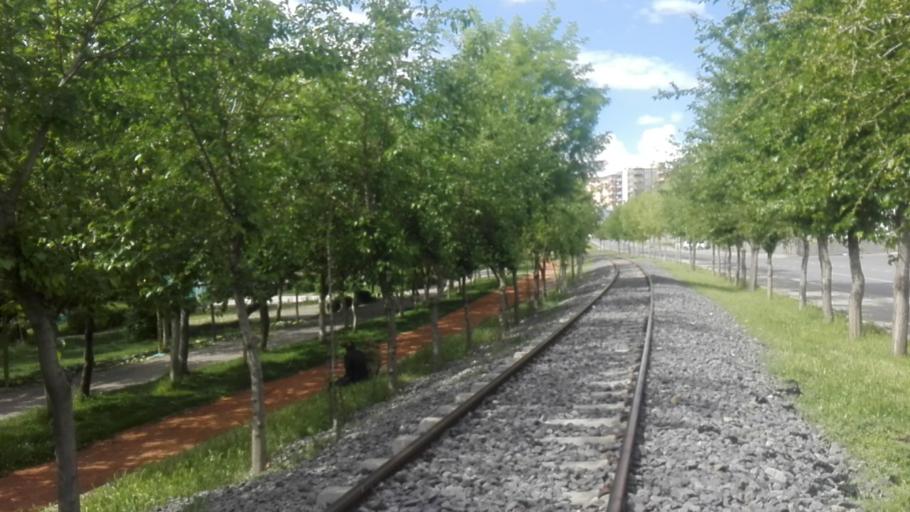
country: TR
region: Batman
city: Batman
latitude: 37.8950
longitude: 41.1463
